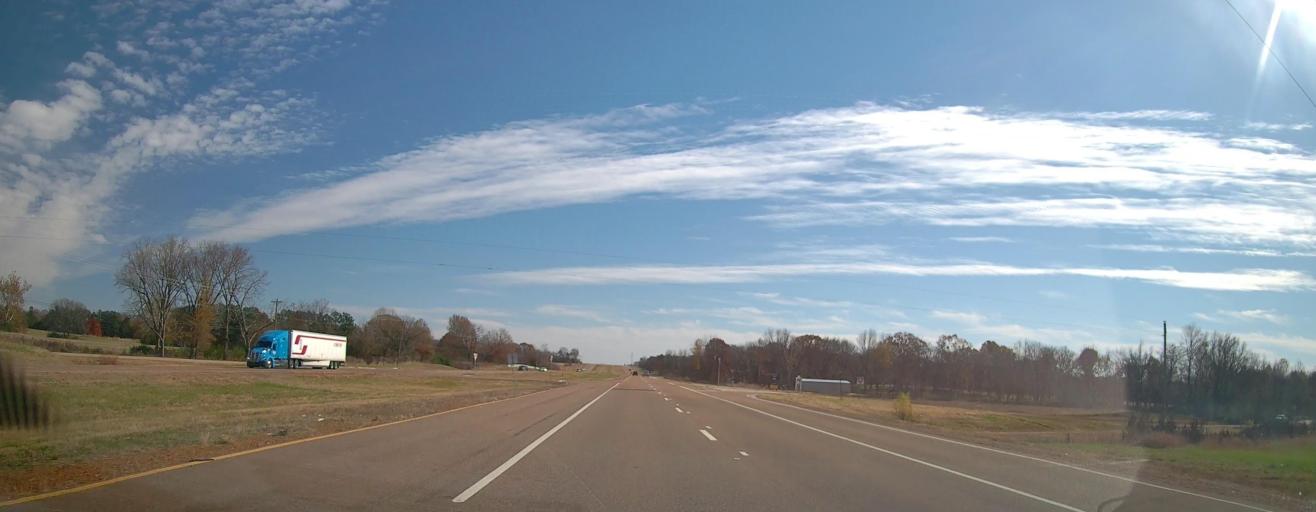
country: US
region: Tennessee
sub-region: Fayette County
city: Piperton
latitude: 34.9739
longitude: -89.5654
